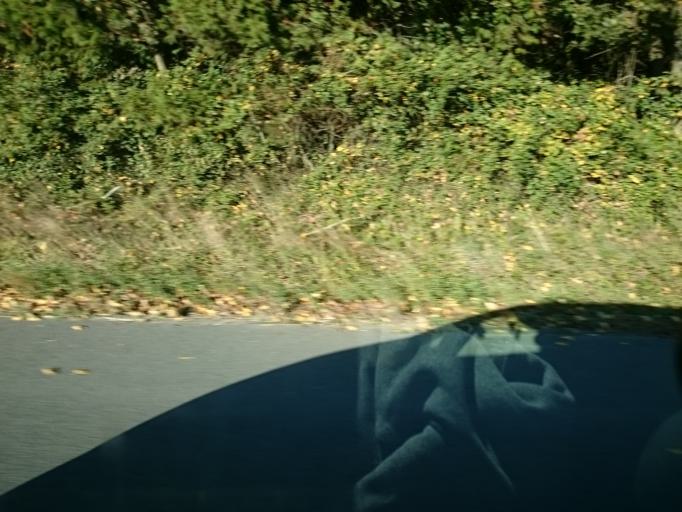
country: FR
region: Brittany
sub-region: Departement d'Ille-et-Vilaine
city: Montauban-de-Bretagne
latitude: 48.2051
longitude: -2.0361
